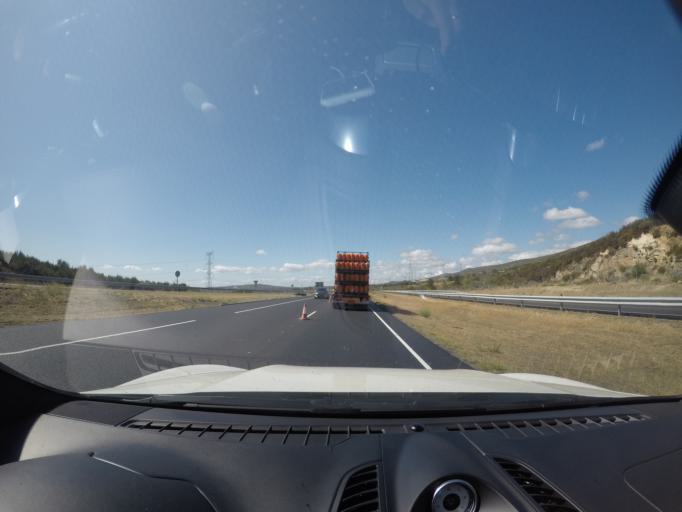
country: ES
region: Castille and Leon
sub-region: Provincia de Zamora
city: Pias
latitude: 42.0377
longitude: -7.0271
